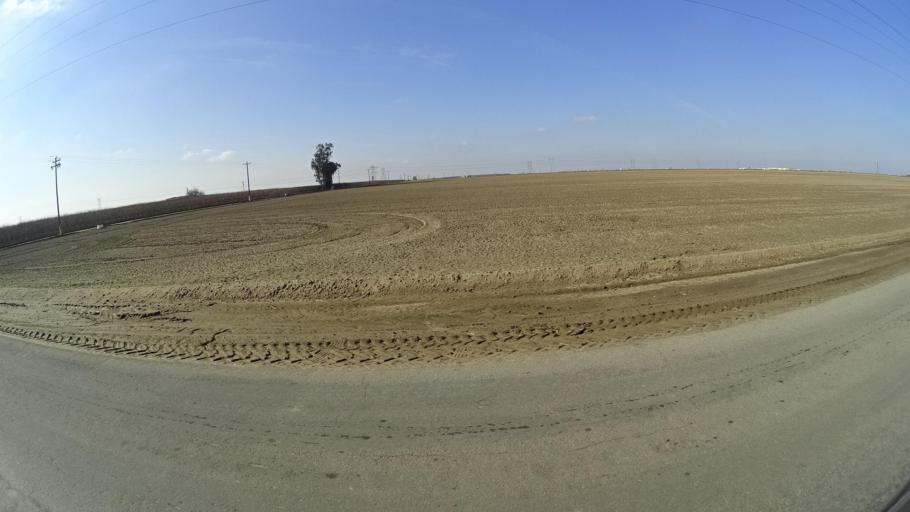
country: US
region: California
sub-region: Kern County
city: Arvin
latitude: 35.2388
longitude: -118.8072
